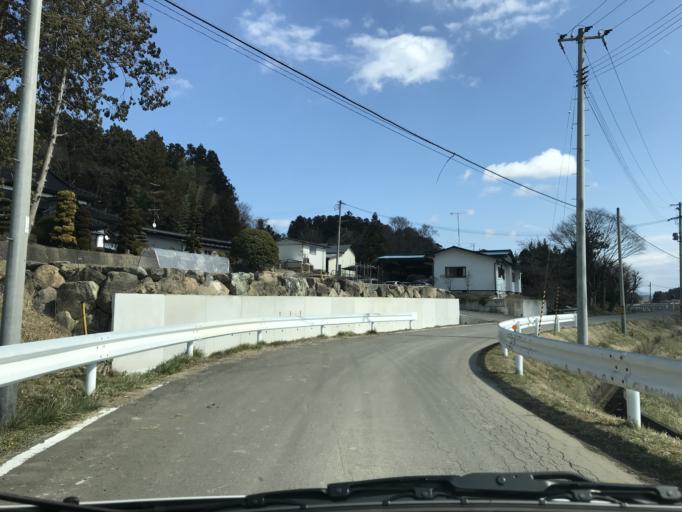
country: JP
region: Miyagi
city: Wakuya
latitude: 38.6795
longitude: 141.1304
